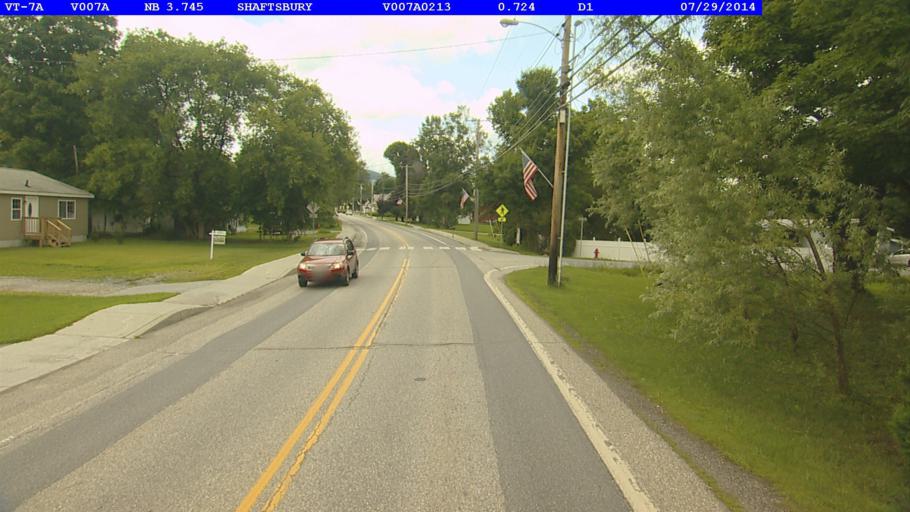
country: US
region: Vermont
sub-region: Bennington County
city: North Bennington
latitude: 42.9432
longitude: -73.2096
